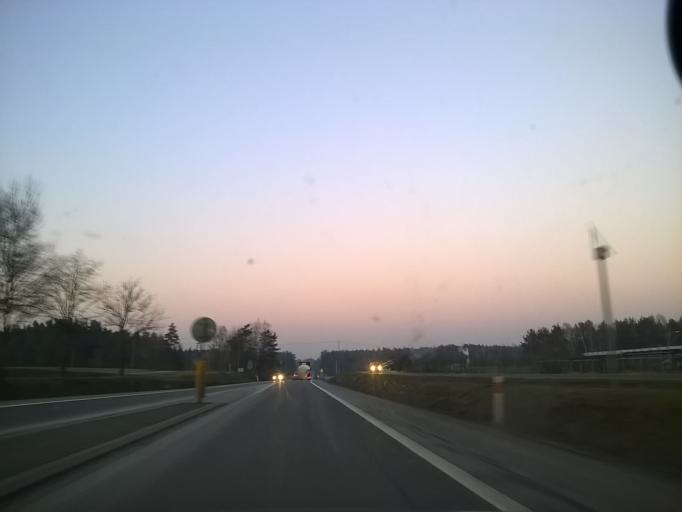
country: PL
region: Warmian-Masurian Voivodeship
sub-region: Powiat olsztynski
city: Barczewo
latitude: 53.7939
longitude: 20.6093
